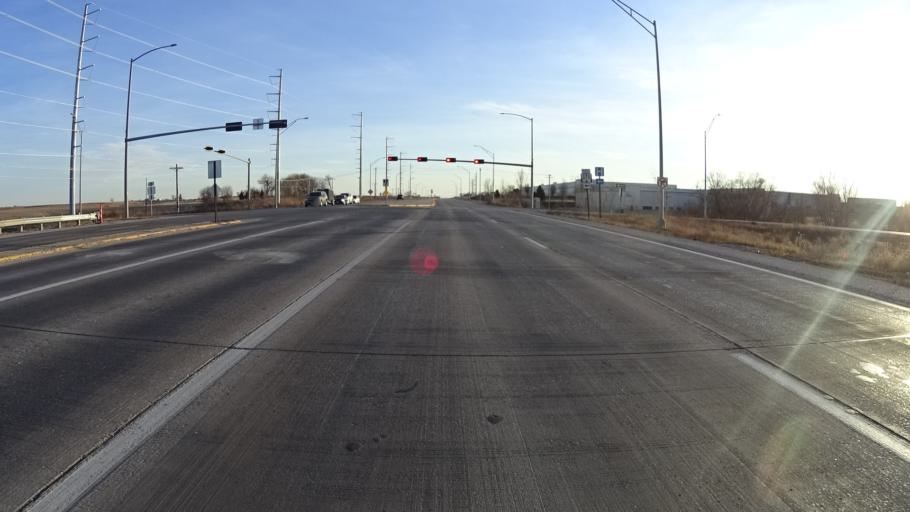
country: US
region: Nebraska
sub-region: Sarpy County
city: Chalco
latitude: 41.1471
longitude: -96.1390
